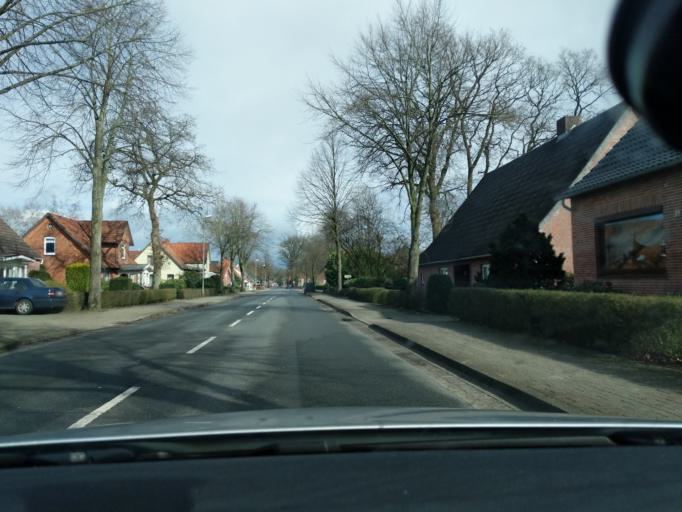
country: DE
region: Lower Saxony
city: Oldendorf
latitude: 53.5896
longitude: 9.2456
